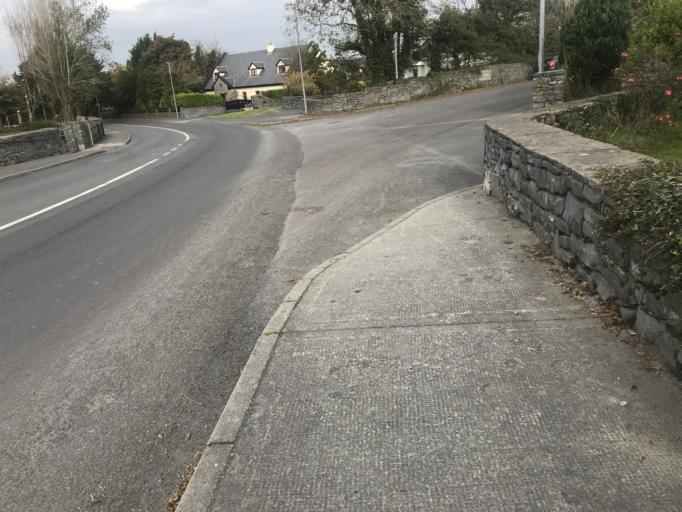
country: IE
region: Connaught
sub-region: County Galway
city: Gaillimh
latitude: 53.2967
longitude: -9.0538
